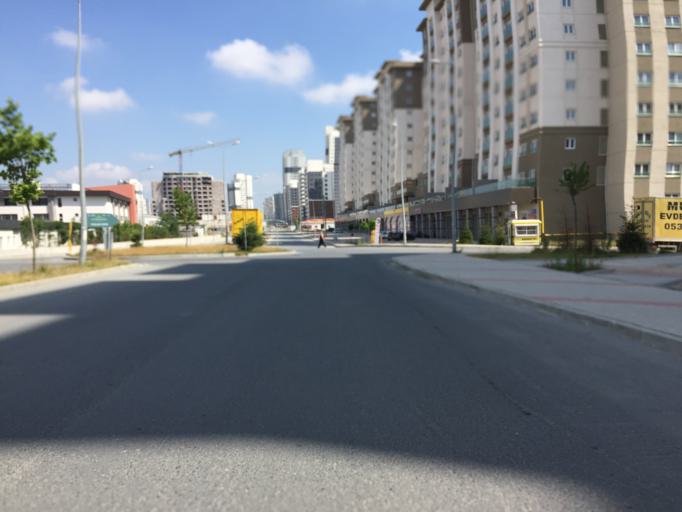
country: TR
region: Istanbul
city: Esenyurt
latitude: 41.0863
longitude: 28.6551
